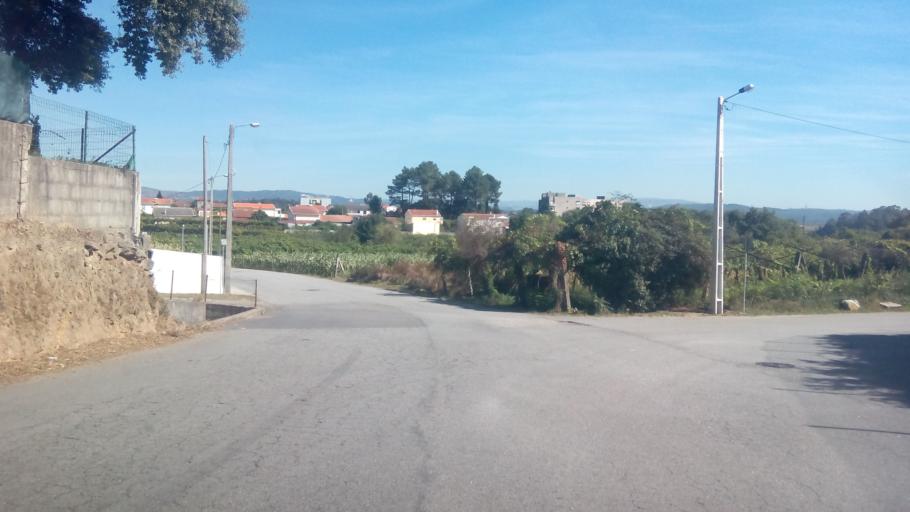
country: PT
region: Porto
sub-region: Paredes
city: Baltar
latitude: 41.1886
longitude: -8.3935
